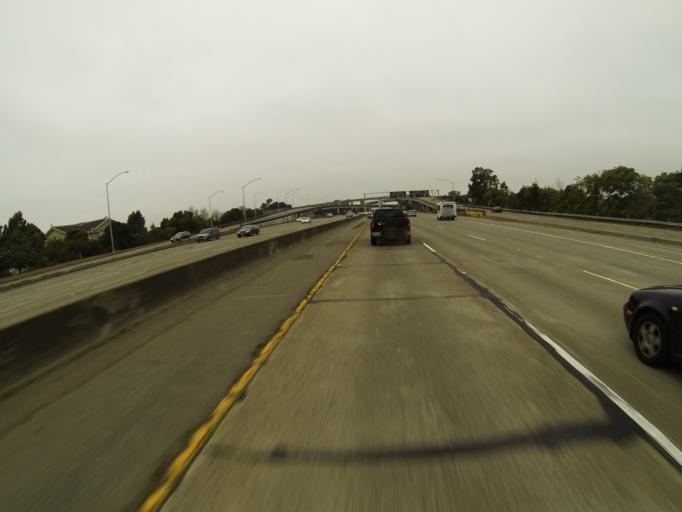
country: US
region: California
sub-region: Alameda County
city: Oakland
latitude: 37.8232
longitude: -122.2630
